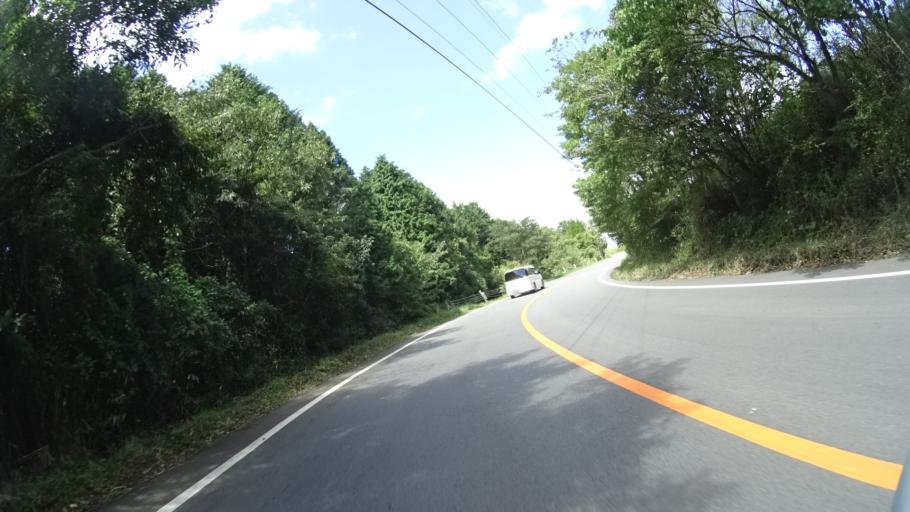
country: JP
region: Kumamoto
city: Aso
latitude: 33.0075
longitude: 131.1175
